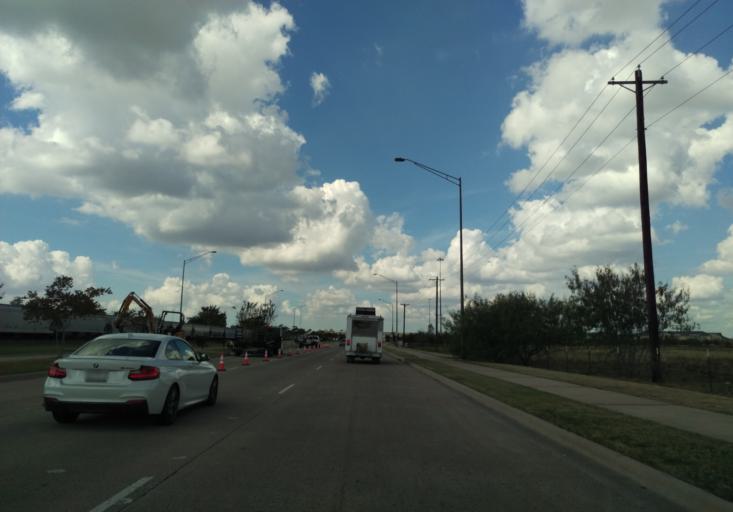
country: US
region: Texas
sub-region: Brazos County
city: College Station
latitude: 30.5826
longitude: -96.3237
